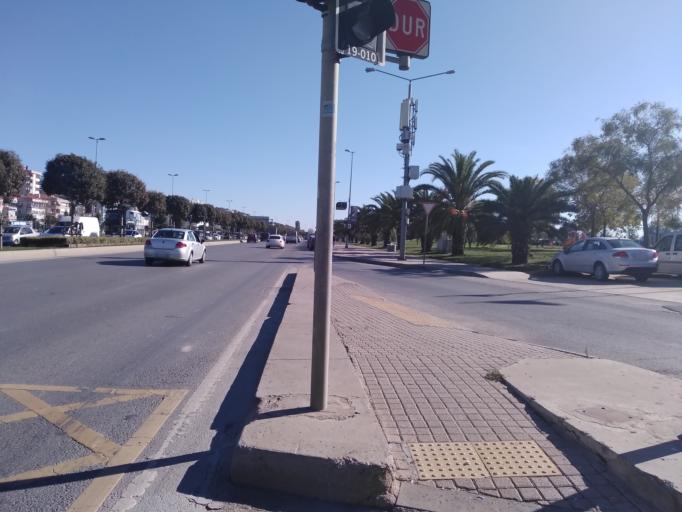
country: TR
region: Istanbul
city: Maltepe
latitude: 40.9178
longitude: 29.1301
